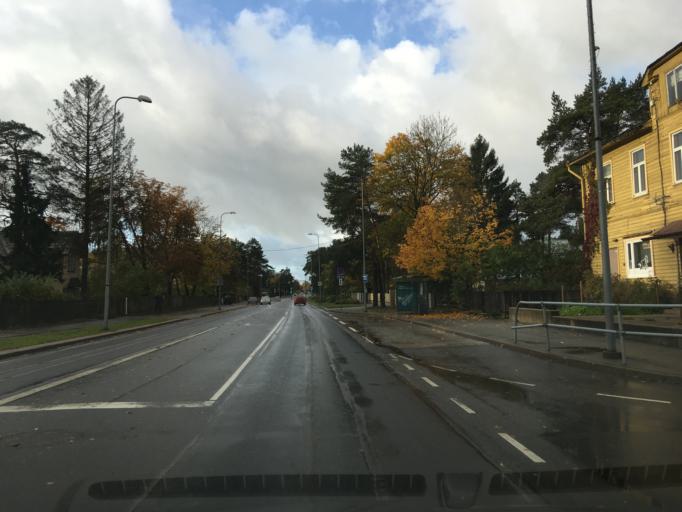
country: EE
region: Harju
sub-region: Saue vald
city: Laagri
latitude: 59.3761
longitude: 24.6494
